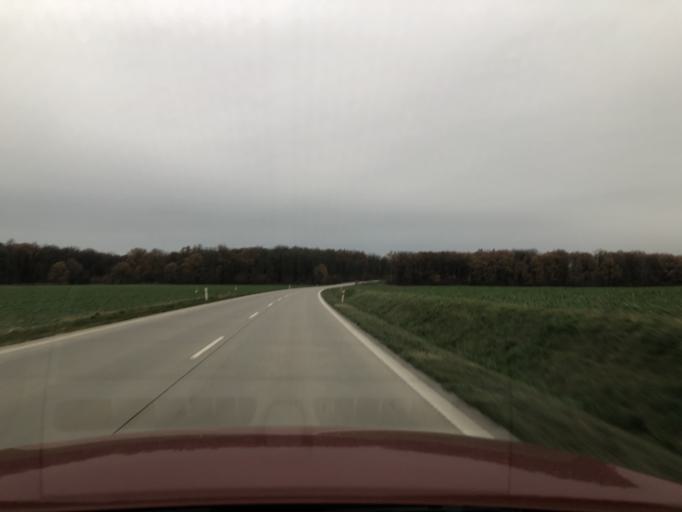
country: PL
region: Lower Silesian Voivodeship
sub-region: Powiat swidnicki
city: Zarow
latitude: 50.9410
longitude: 16.4739
